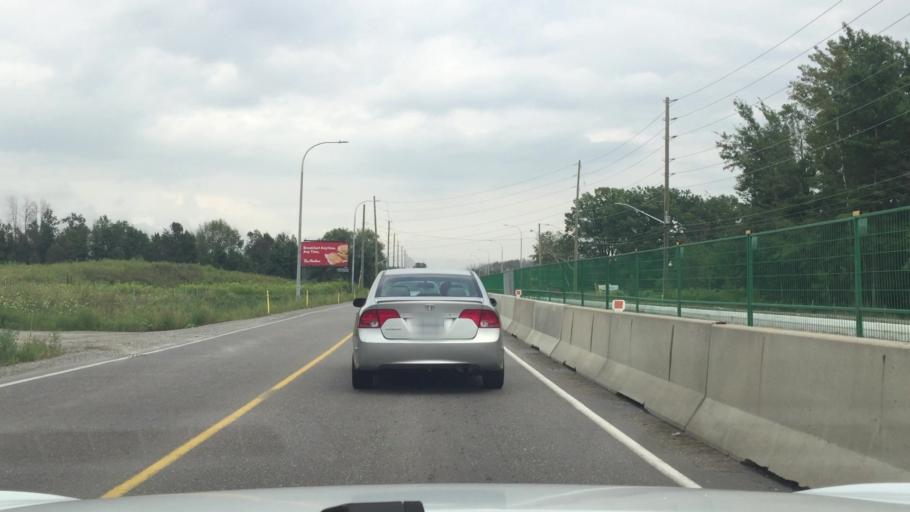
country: CA
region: Ontario
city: Ajax
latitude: 43.8549
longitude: -78.9690
